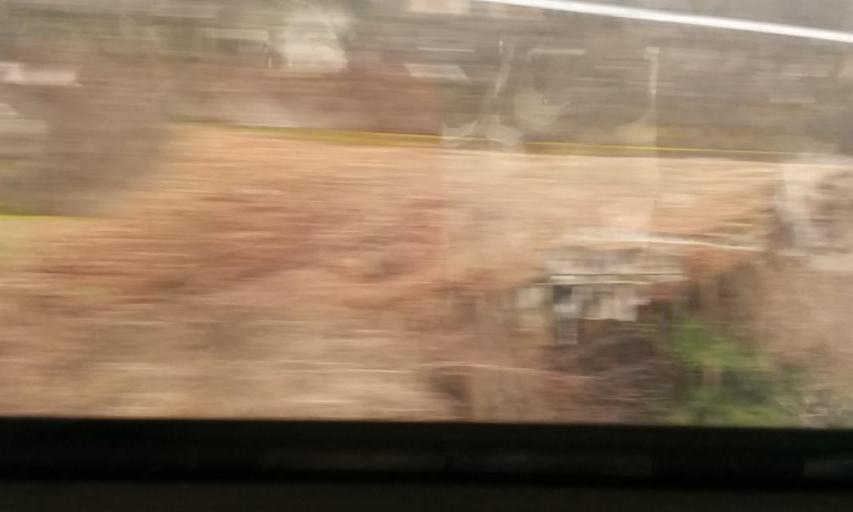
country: JP
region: Nagano
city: Ina
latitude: 35.8834
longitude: 137.7578
